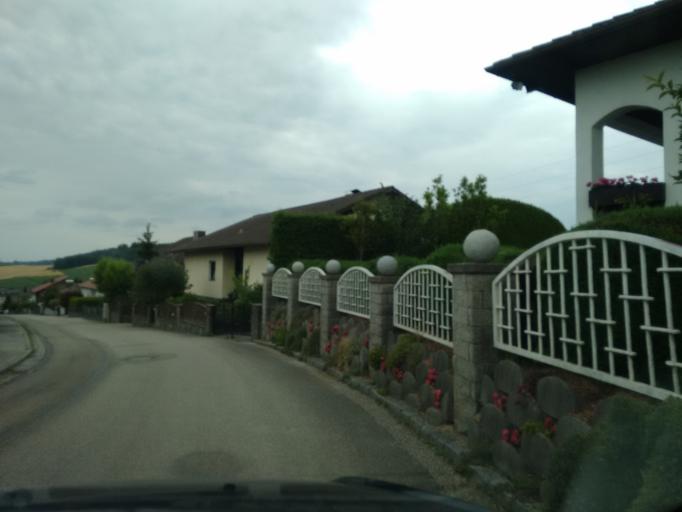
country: AT
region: Upper Austria
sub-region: Politischer Bezirk Grieskirchen
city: Bad Schallerbach
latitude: 48.2032
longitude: 13.9511
